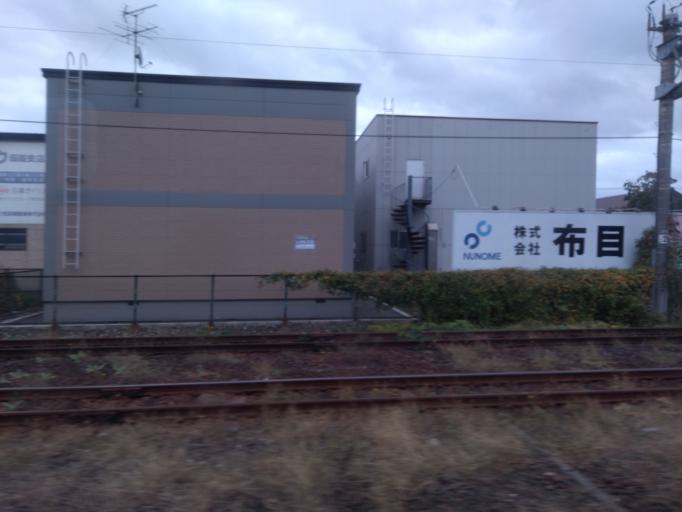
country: JP
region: Hokkaido
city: Hakodate
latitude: 41.7799
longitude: 140.7290
